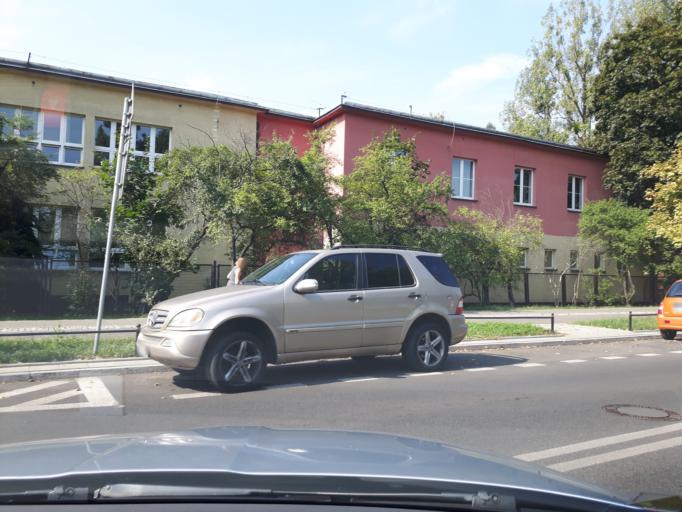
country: PL
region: Masovian Voivodeship
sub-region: Warszawa
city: Praga Polnoc
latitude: 52.2648
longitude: 21.0323
